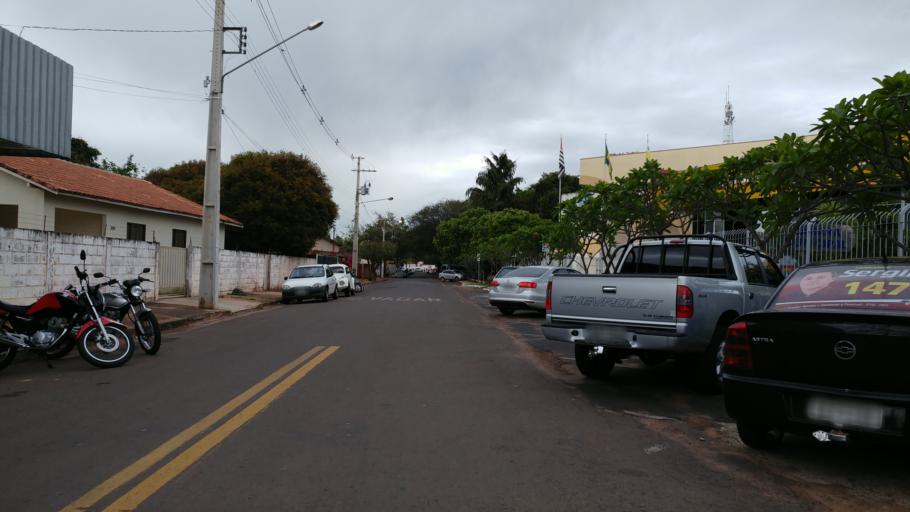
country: BR
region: Sao Paulo
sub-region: Paraguacu Paulista
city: Paraguacu Paulista
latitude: -22.4221
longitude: -50.5814
